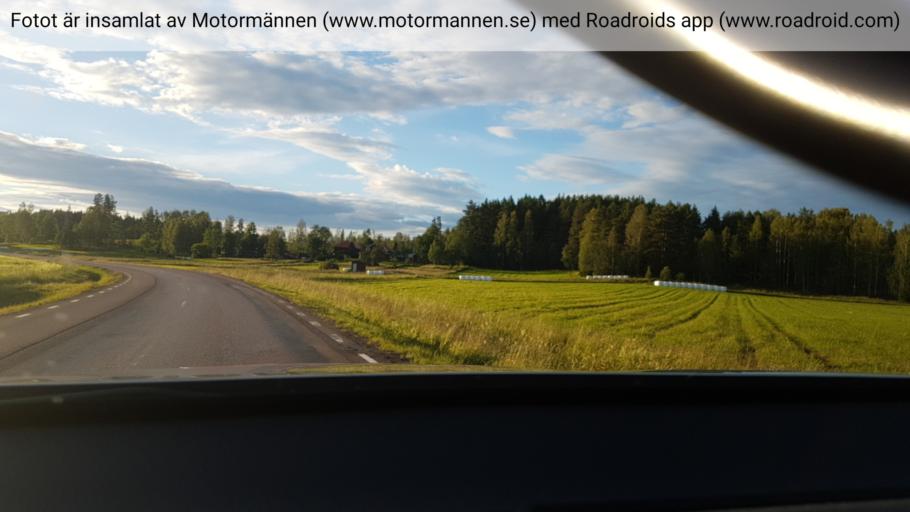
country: SE
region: Vaermland
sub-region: Sunne Kommun
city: Sunne
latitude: 59.9519
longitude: 13.1530
